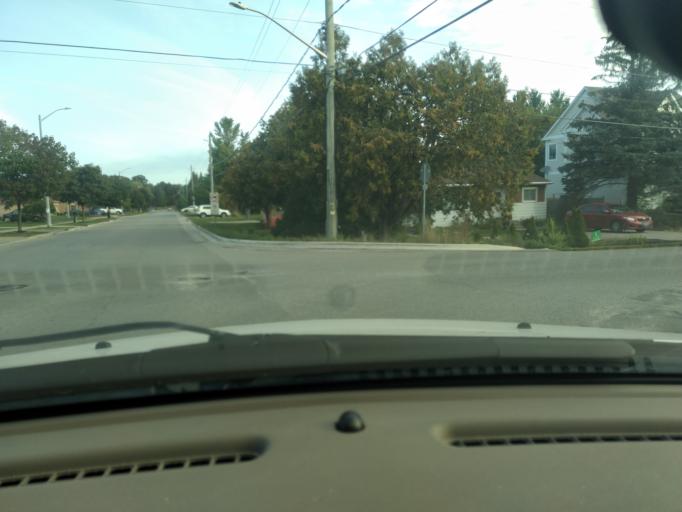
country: CA
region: Ontario
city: Innisfil
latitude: 44.3164
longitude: -79.5526
